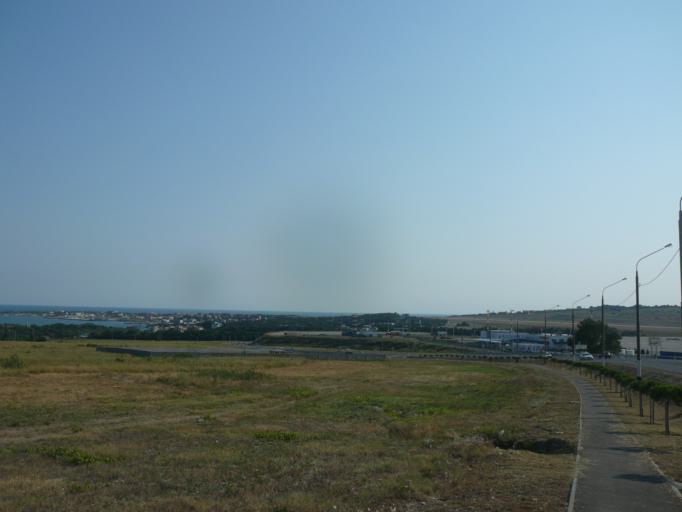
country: RU
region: Krasnodarskiy
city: Gelendzhik
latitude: 44.5972
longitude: 38.0289
